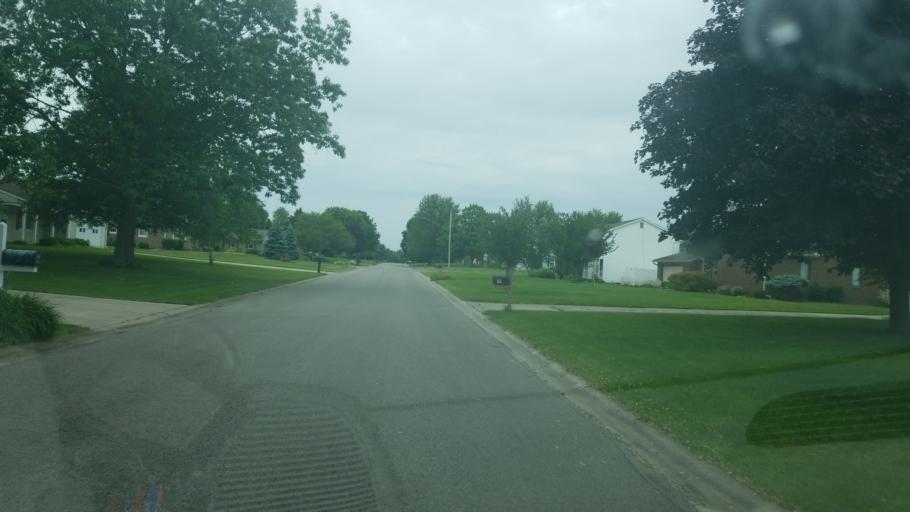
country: US
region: Ohio
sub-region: Crawford County
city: Bucyrus
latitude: 40.7959
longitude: -82.9905
